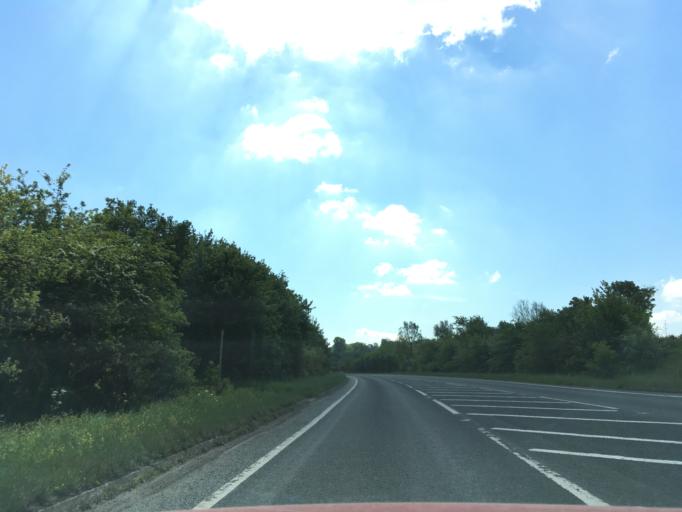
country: GB
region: England
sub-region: Northamptonshire
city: Brackley
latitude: 52.0247
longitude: -1.1573
